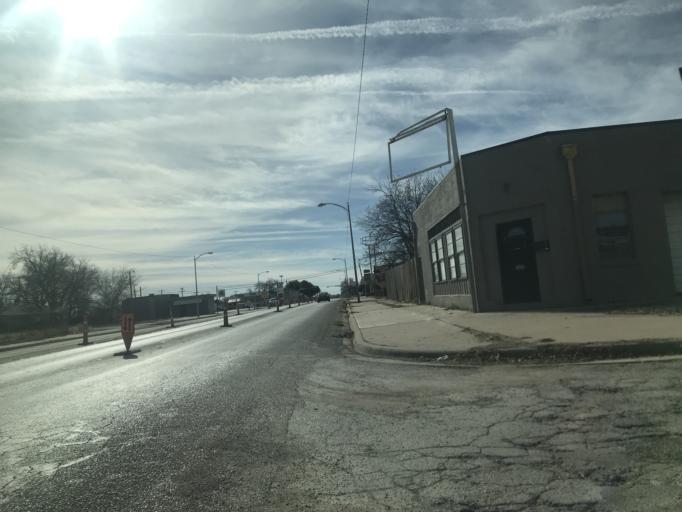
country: US
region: Texas
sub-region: Taylor County
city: Abilene
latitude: 32.4447
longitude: -99.7378
